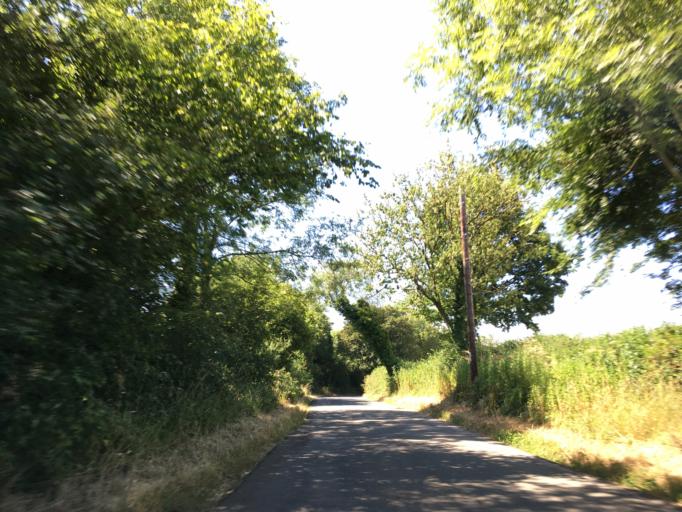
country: GB
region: England
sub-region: Wiltshire
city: Luckington
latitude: 51.5511
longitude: -2.2306
